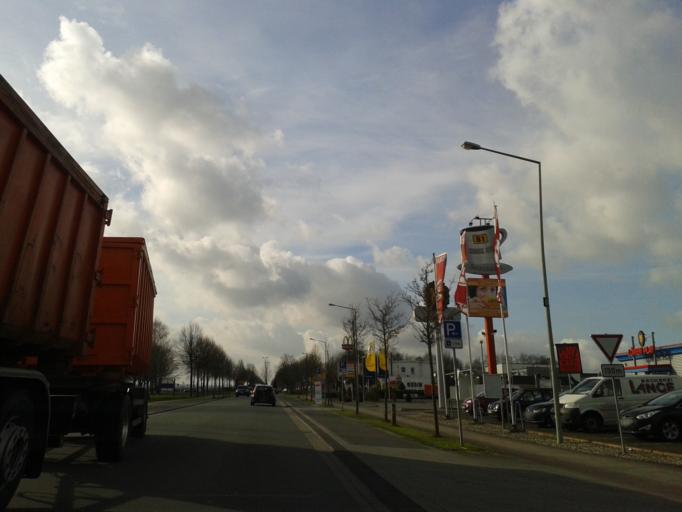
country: DE
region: North Rhine-Westphalia
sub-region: Regierungsbezirk Detmold
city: Salzkotten
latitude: 51.6670
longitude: 8.5912
